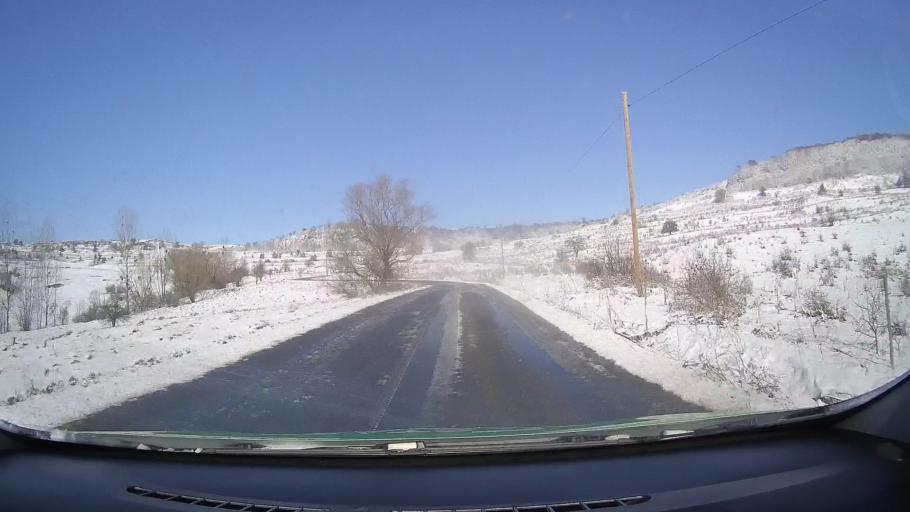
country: RO
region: Sibiu
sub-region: Comuna Avrig
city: Avrig
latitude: 45.7732
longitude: 24.3828
